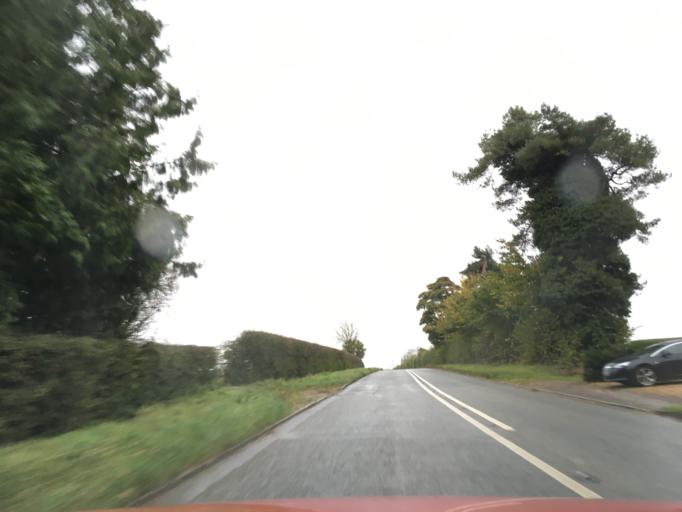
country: GB
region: England
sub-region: West Berkshire
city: Wickham
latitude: 51.4543
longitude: -1.4667
